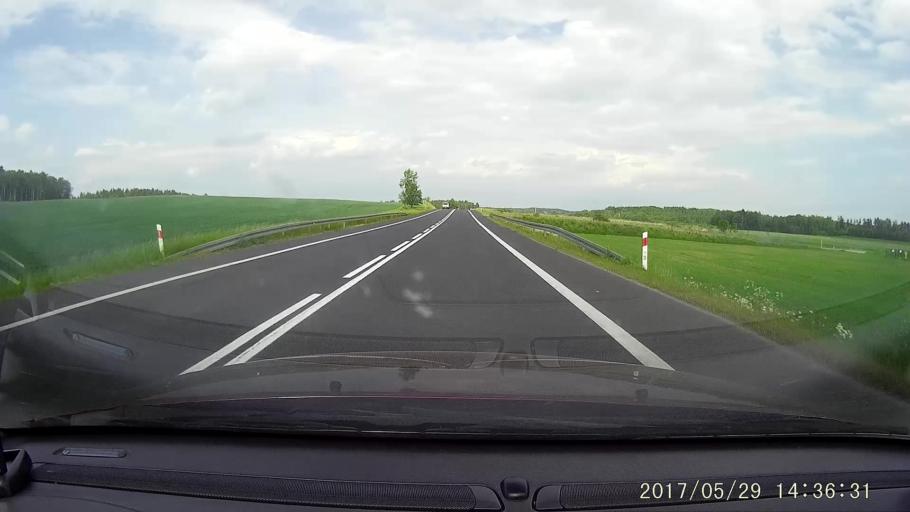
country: PL
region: Lower Silesian Voivodeship
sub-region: Powiat lubanski
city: Siekierczyn
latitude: 51.2085
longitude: 15.1561
